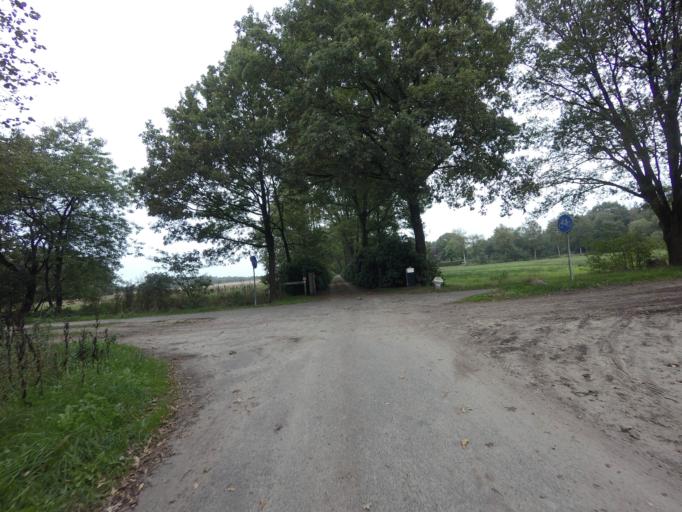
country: NL
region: Drenthe
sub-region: Gemeente Westerveld
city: Dwingeloo
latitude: 52.9073
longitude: 6.4712
